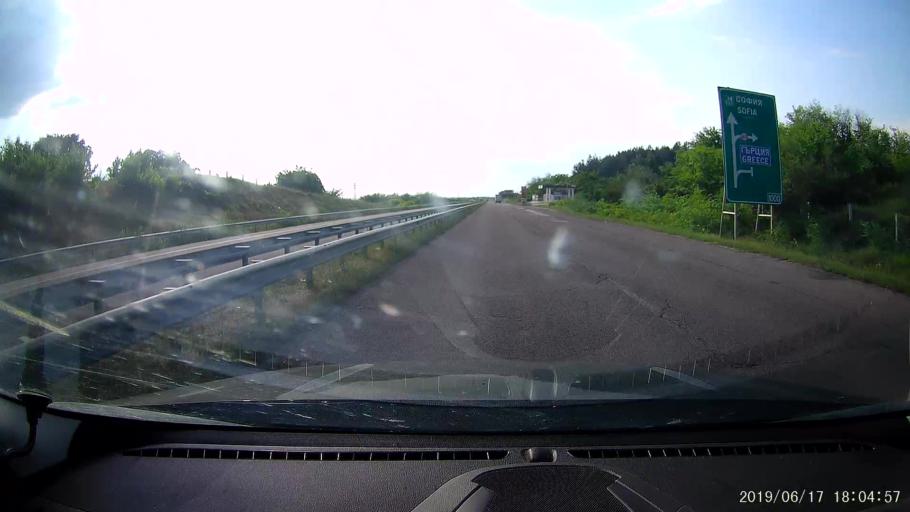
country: BG
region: Khaskovo
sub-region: Obshtina Svilengrad
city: Svilengrad
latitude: 41.7918
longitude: 26.1872
